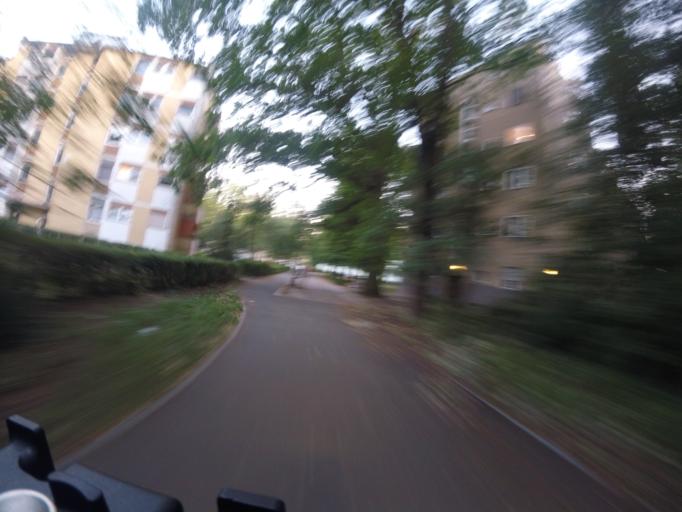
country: DE
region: Berlin
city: Siemensstadt
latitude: 52.5429
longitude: 13.2719
